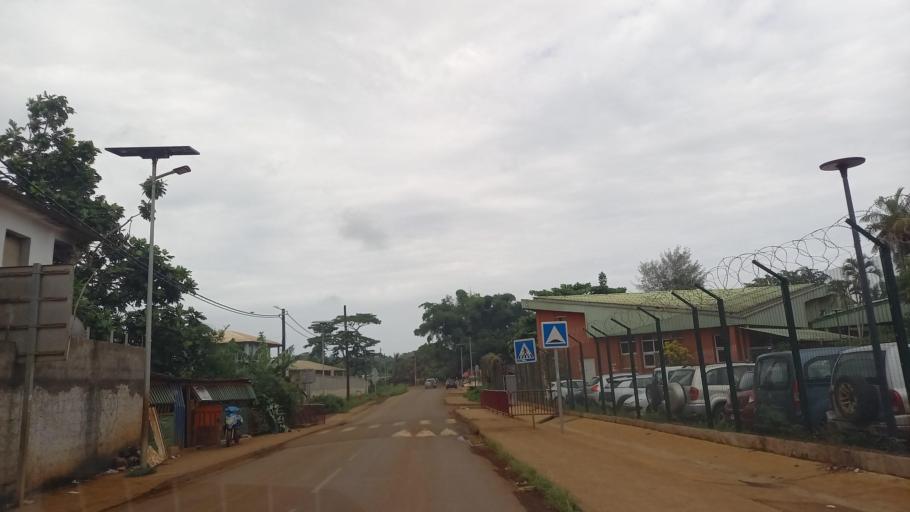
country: YT
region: Chiconi
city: Chiconi
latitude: -12.8232
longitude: 45.1312
